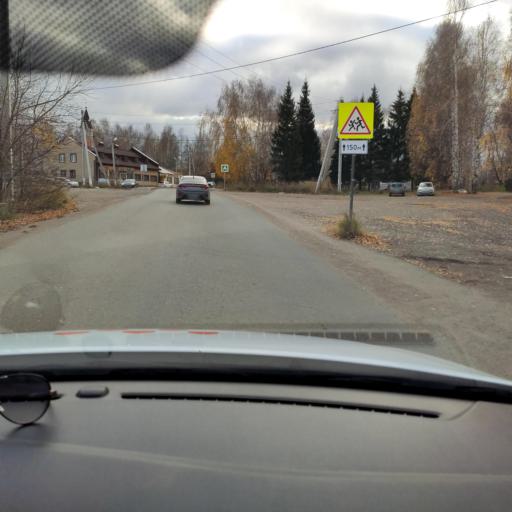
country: RU
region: Tatarstan
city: Stolbishchi
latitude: 55.7422
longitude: 49.2732
